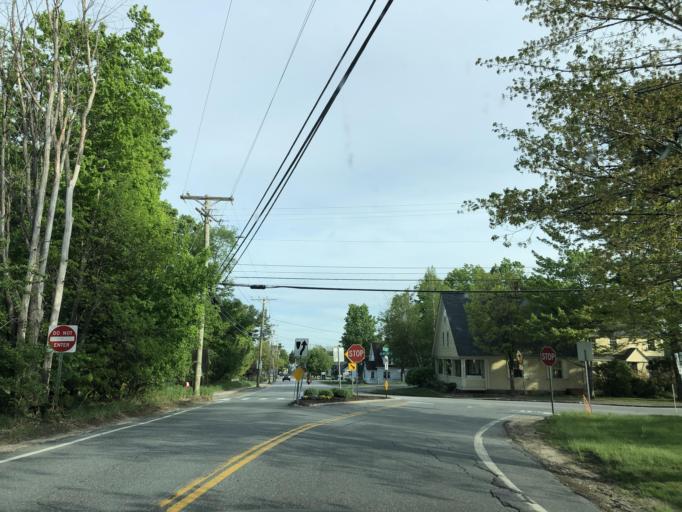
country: US
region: New Hampshire
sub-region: Merrimack County
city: New London
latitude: 43.4213
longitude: -71.9924
